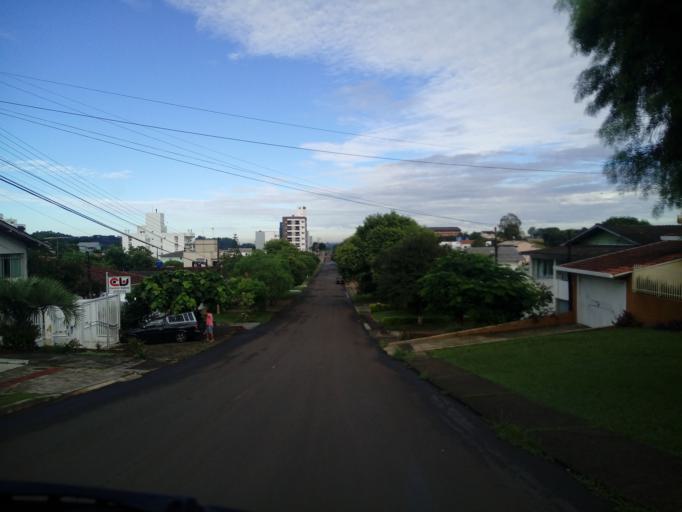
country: BR
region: Santa Catarina
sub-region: Chapeco
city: Chapeco
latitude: -27.1072
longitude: -52.6253
